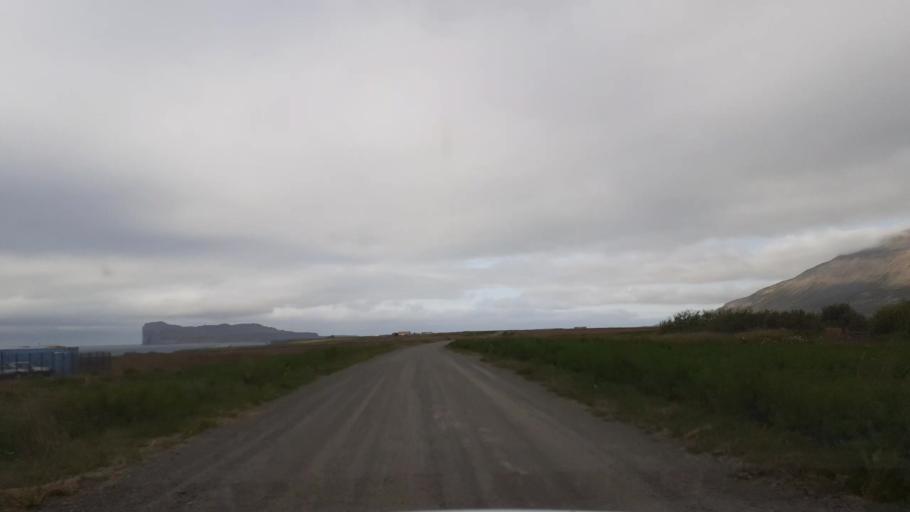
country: IS
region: Northwest
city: Saudarkrokur
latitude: 65.9013
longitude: -19.4220
